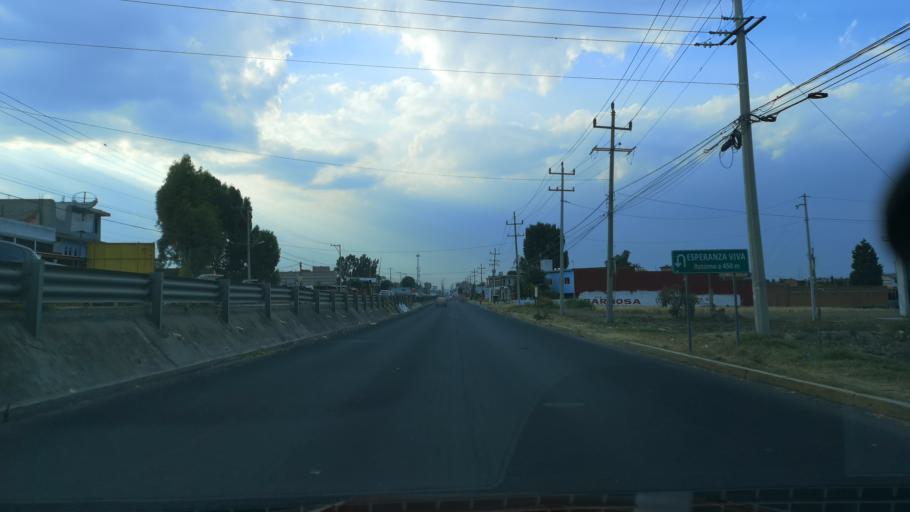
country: MX
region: Puebla
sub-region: Juan C. Bonilla
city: Santa Maria Zacatepec
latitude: 19.1150
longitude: -98.3581
